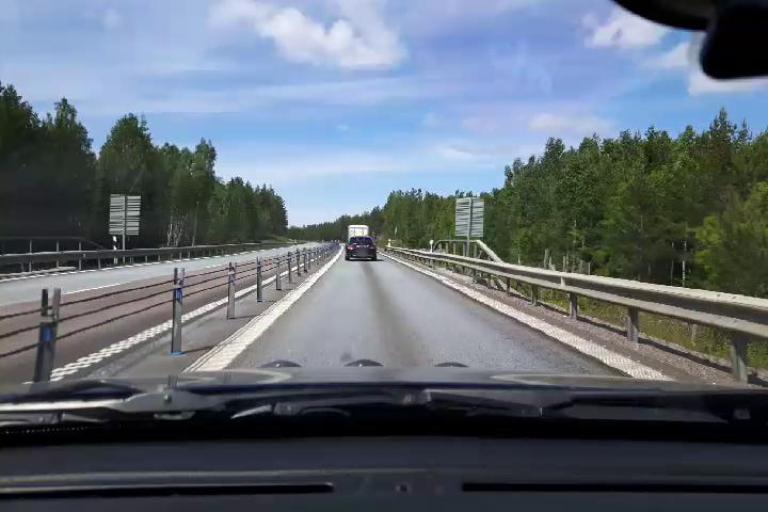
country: SE
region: Gaevleborg
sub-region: Gavle Kommun
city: Gavle
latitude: 60.7059
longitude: 17.0860
